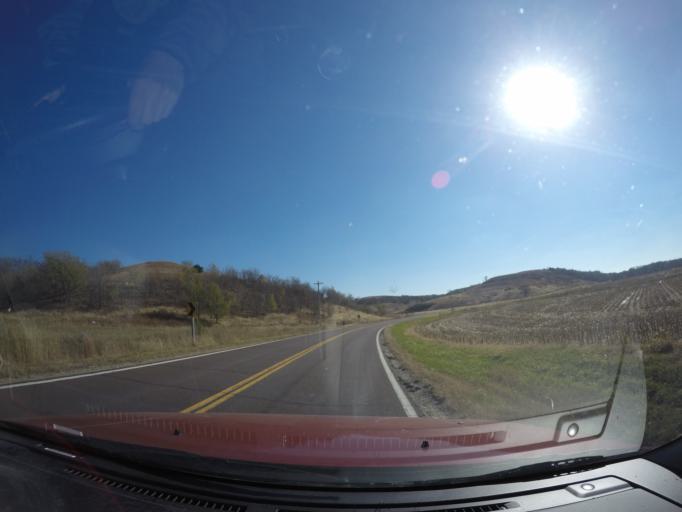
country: US
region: Kansas
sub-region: Geary County
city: Grandview Plaza
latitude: 39.0075
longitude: -96.7318
